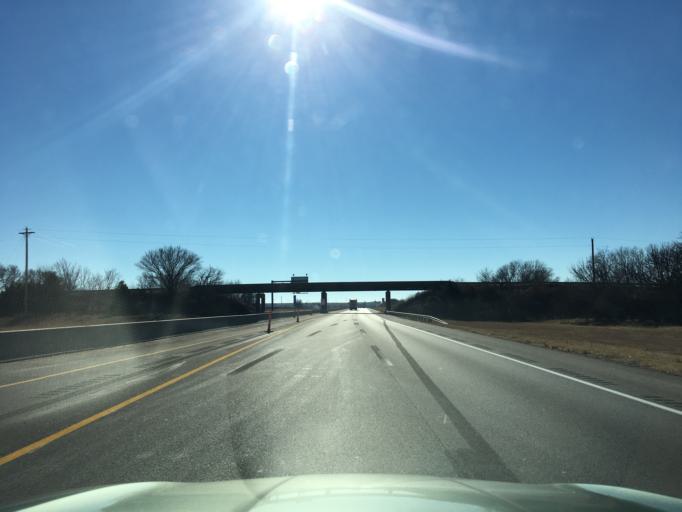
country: US
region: Kansas
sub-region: Sumner County
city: Wellington
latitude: 37.2337
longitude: -97.3389
